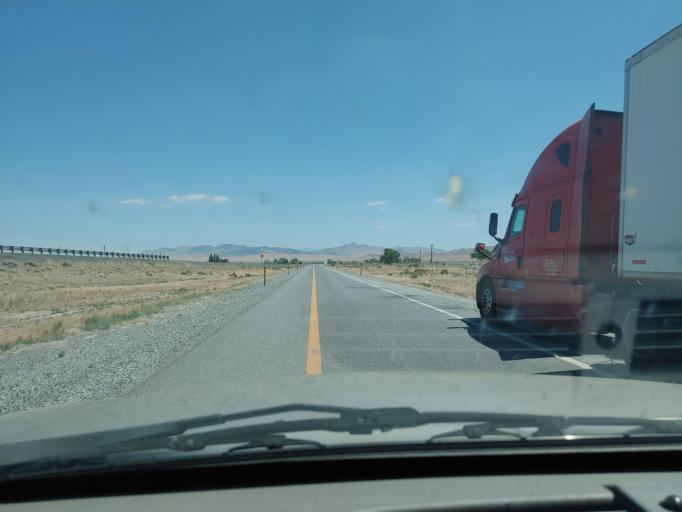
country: US
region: Nevada
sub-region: Humboldt County
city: Winnemucca
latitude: 40.6561
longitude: -118.1451
